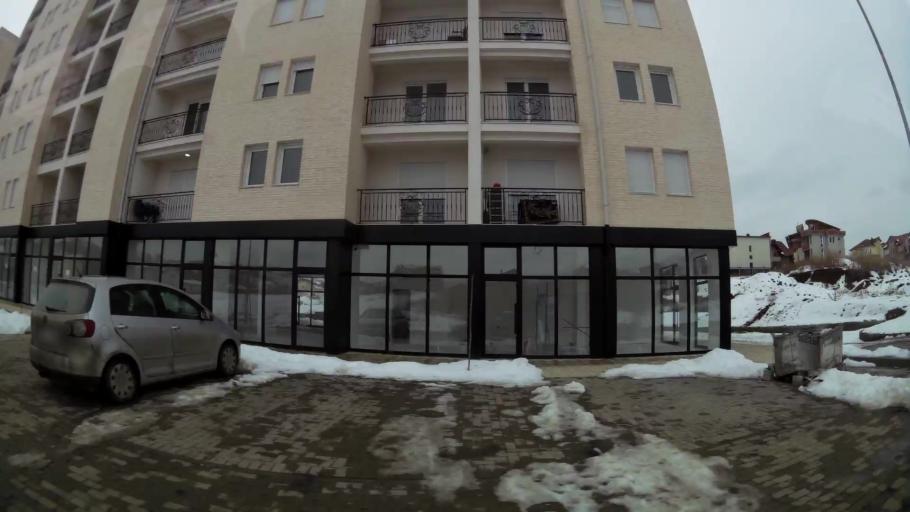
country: XK
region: Pristina
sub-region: Komuna e Prishtines
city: Pristina
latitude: 42.6438
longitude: 21.1819
